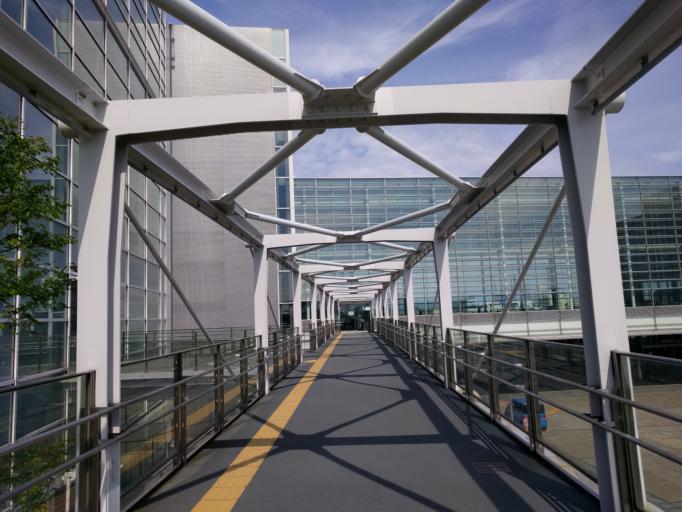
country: JP
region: Niigata
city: Niigata-shi
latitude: 37.9253
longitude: 139.0601
